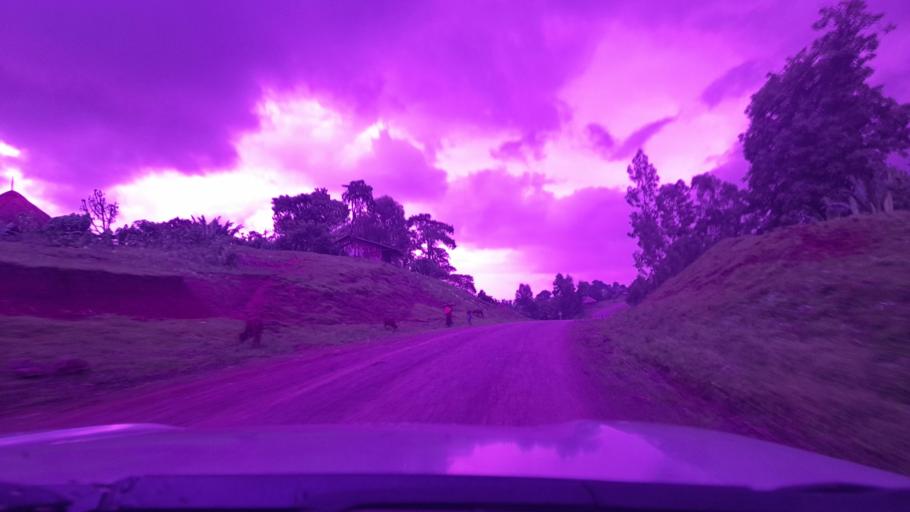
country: ET
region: Southern Nations, Nationalities, and People's Region
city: Mizan Teferi
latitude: 6.8944
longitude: 35.8463
